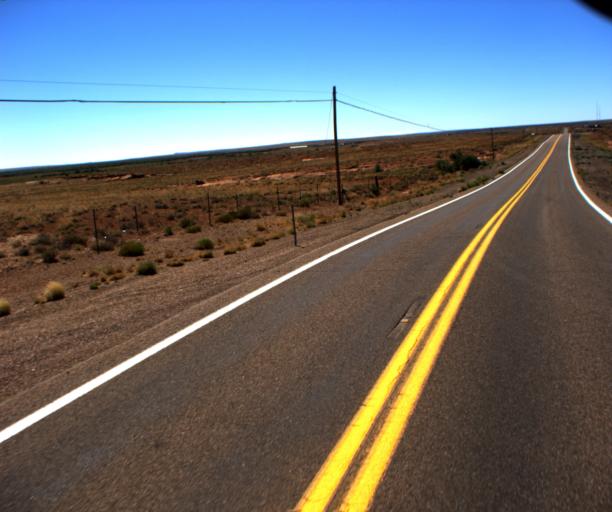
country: US
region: Arizona
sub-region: Navajo County
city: Winslow
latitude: 34.9938
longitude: -110.6700
